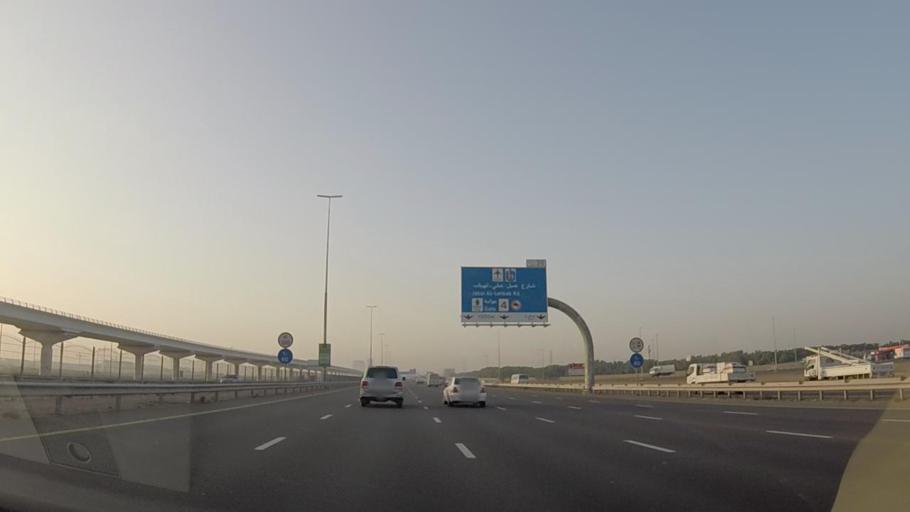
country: AE
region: Dubai
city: Dubai
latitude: 25.0131
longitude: 55.0971
